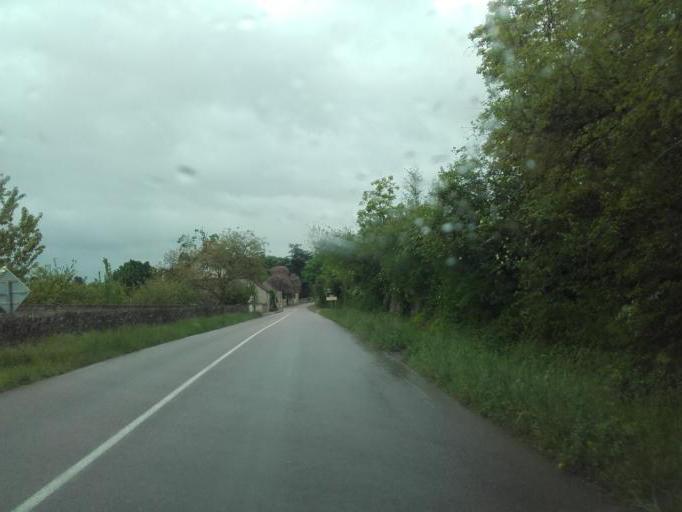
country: FR
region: Bourgogne
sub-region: Departement de Saone-et-Loire
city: Fontaines
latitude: 46.8513
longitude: 4.7544
